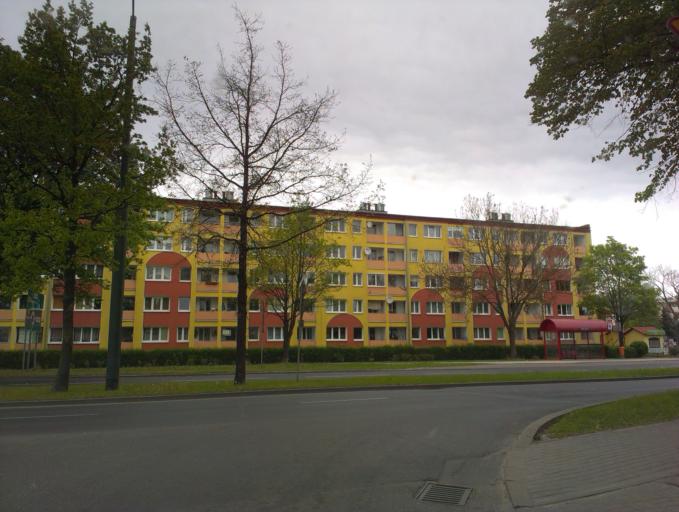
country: PL
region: West Pomeranian Voivodeship
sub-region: Powiat kolobrzeski
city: Kolobrzeg
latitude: 54.1756
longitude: 15.5903
